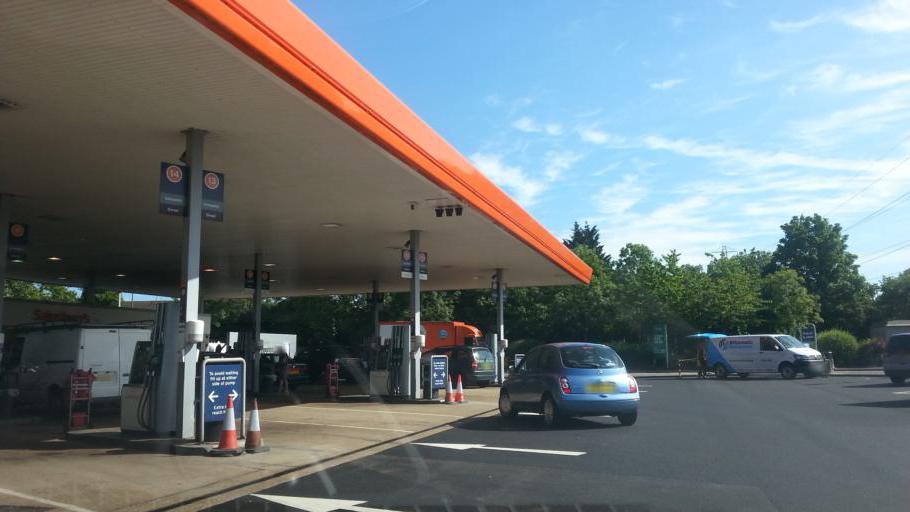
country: GB
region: England
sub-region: Hertfordshire
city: Shenley AV
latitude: 51.7167
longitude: -0.2811
